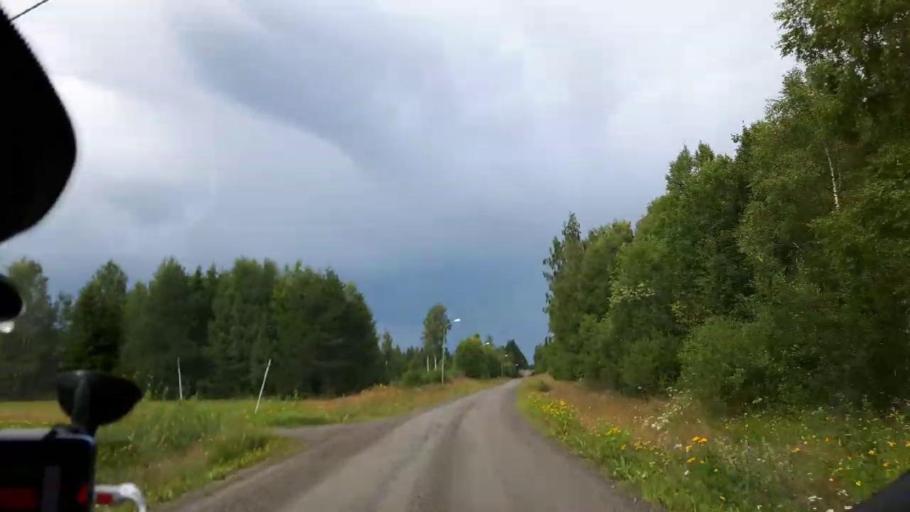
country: SE
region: Jaemtland
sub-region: Stroemsunds Kommun
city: Stroemsund
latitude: 64.0584
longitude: 15.8902
